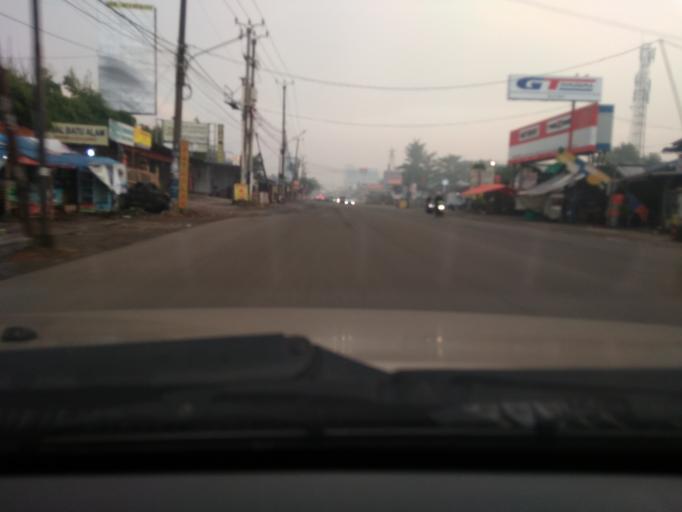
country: ID
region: West Java
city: Serpong
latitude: -6.3256
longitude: 106.6839
